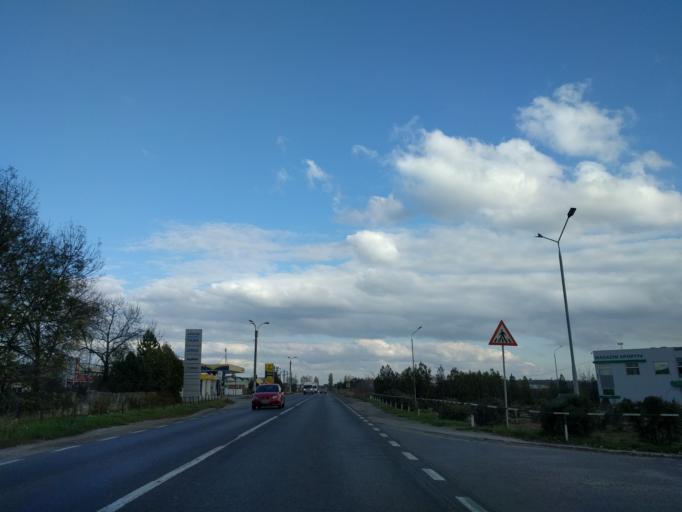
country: RO
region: Ilfov
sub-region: Comuna Ganeasa
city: Ganeasa
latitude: 44.4533
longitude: 26.2606
